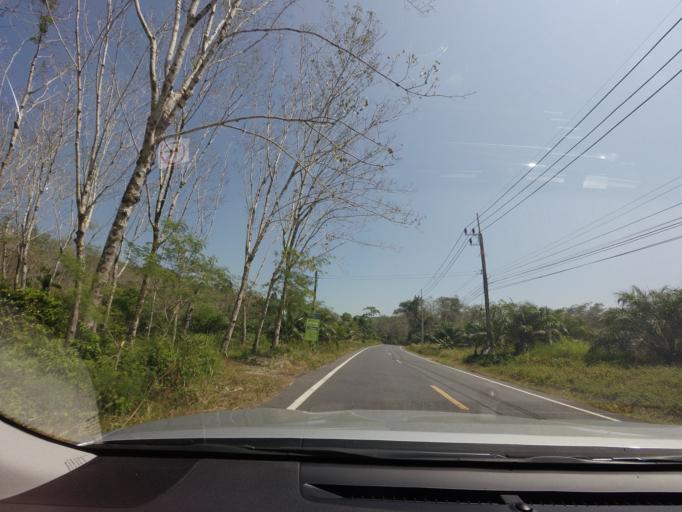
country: TH
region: Phangnga
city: Takua Thung
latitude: 8.2537
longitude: 98.4193
